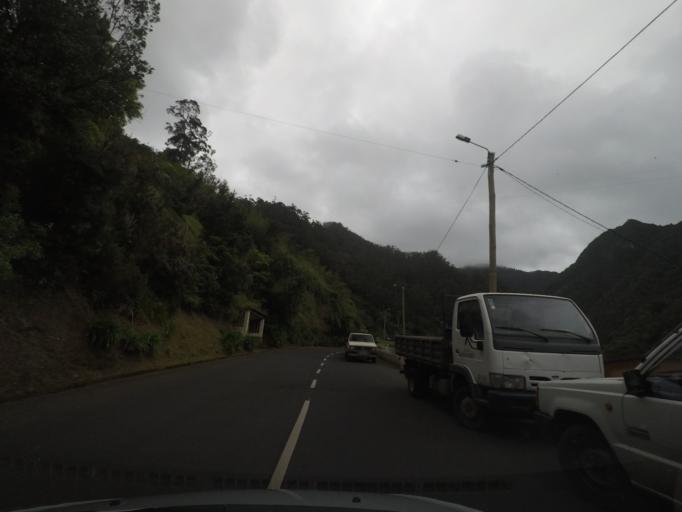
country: PT
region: Madeira
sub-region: Santana
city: Santana
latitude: 32.7514
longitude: -16.8395
